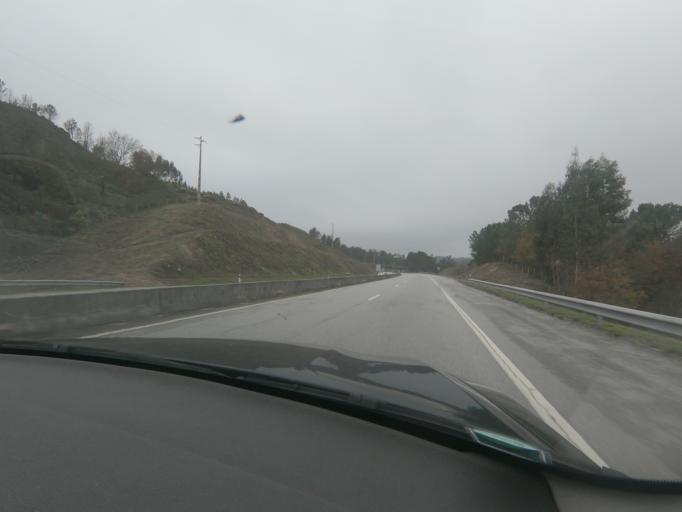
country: PT
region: Viseu
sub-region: Viseu
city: Viseu
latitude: 40.6067
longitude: -7.9713
